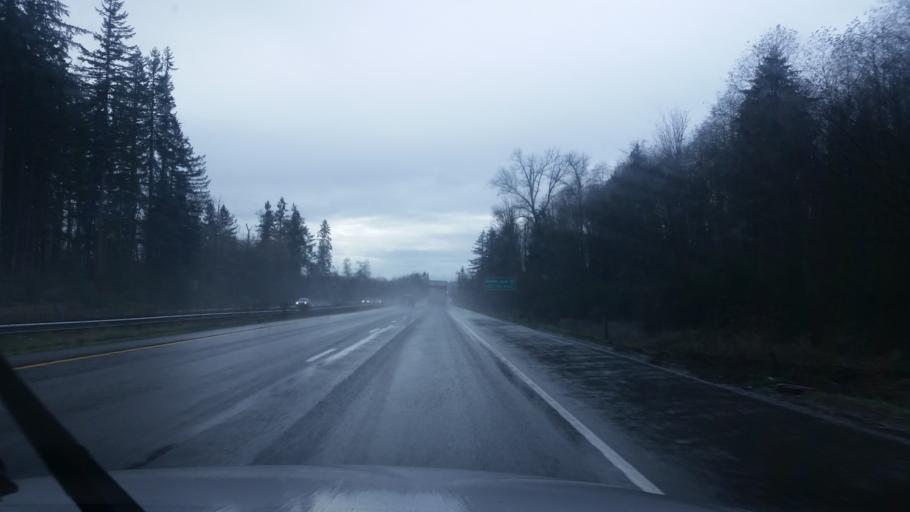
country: US
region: Washington
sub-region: King County
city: Hobart
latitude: 47.4208
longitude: -122.0022
